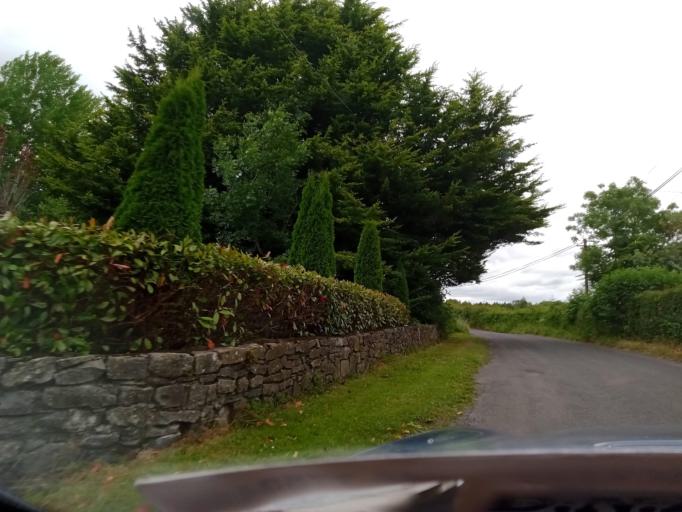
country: IE
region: Leinster
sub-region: Kilkenny
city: Thomastown
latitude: 52.5725
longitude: -7.1944
